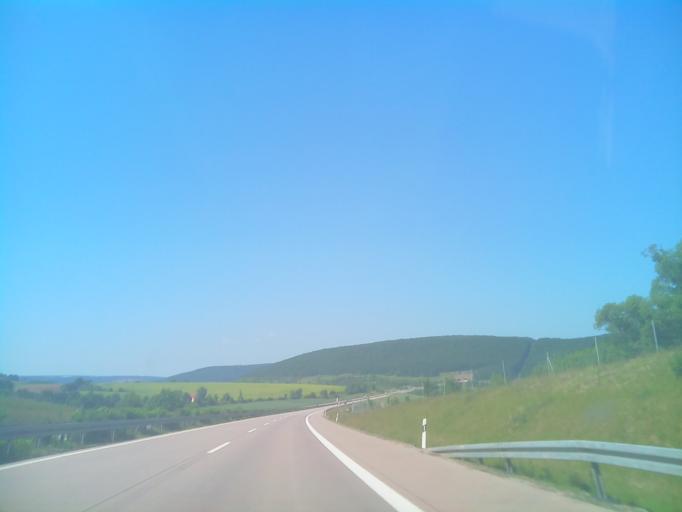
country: DE
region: Thuringia
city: Wolfershausen
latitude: 50.4900
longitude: 10.4415
